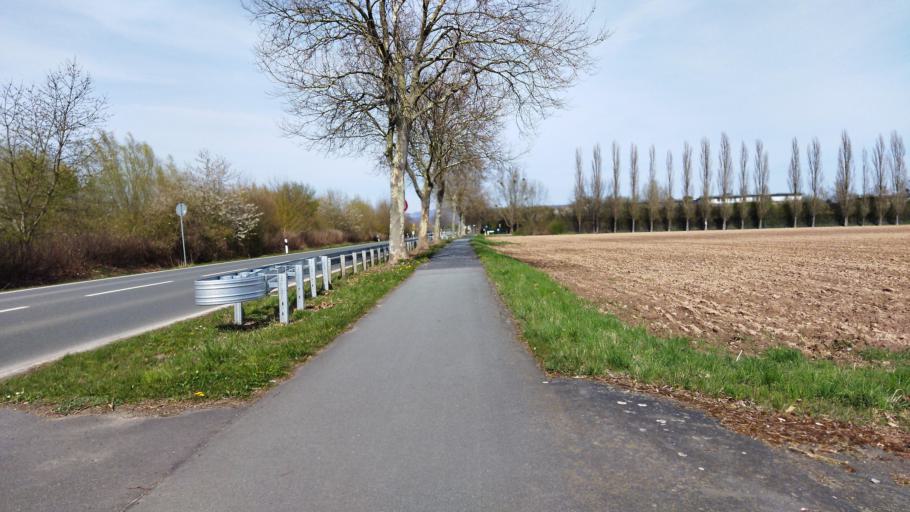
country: DE
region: Lower Saxony
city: Hameln
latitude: 52.0752
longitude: 9.3780
